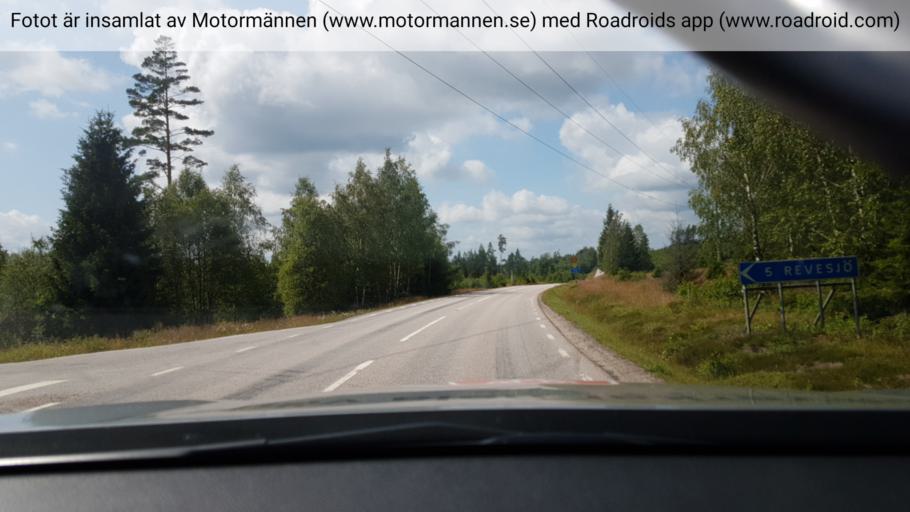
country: SE
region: Vaestra Goetaland
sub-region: Svenljunga Kommun
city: Svenljunga
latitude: 57.4826
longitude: 13.0127
